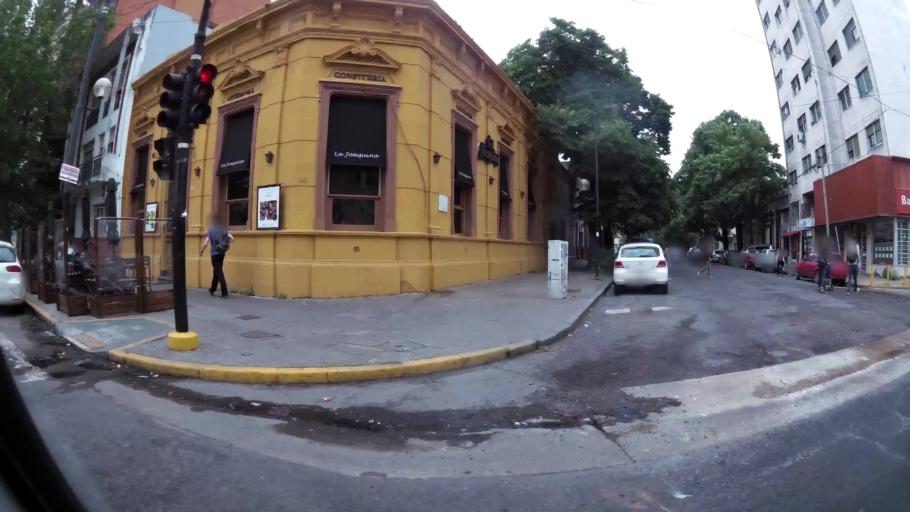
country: AR
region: Buenos Aires
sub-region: Partido de La Plata
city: La Plata
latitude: -34.9235
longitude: -57.9542
